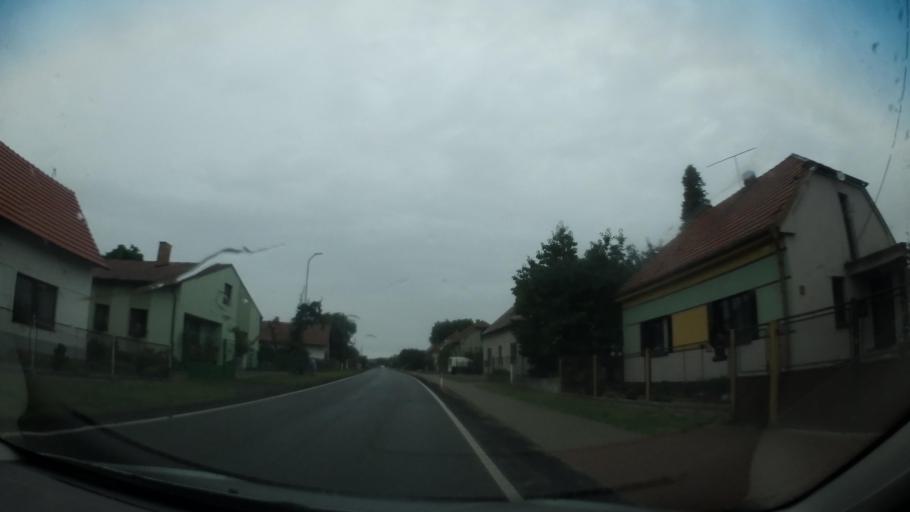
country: CZ
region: Central Bohemia
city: Milovice
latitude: 50.2391
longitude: 14.9544
